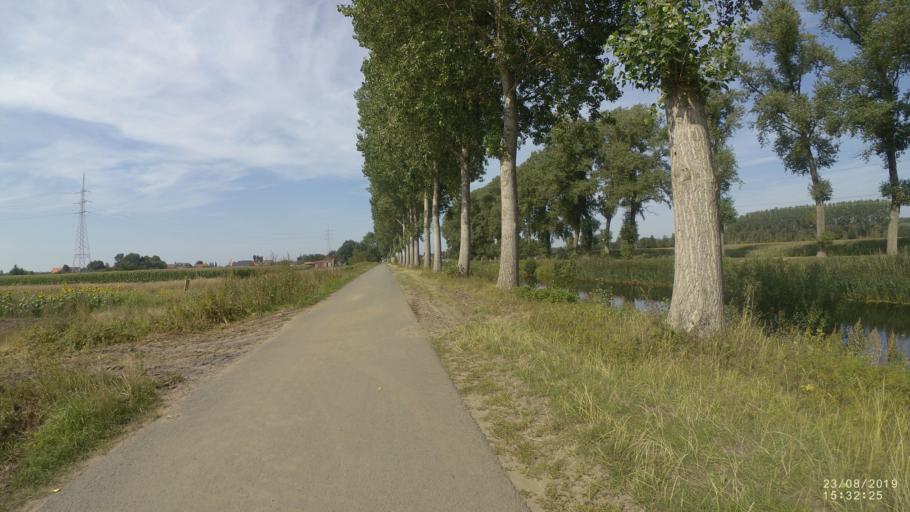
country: BE
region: Flanders
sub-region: Provincie Oost-Vlaanderen
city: Eeklo
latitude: 51.1557
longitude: 3.5488
